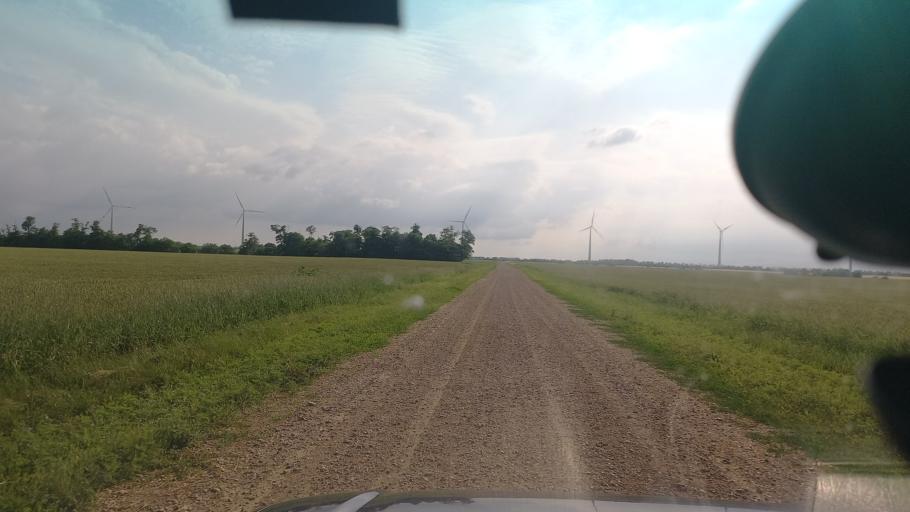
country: RU
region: Adygeya
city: Giaginskaya
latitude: 44.9545
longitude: 40.0947
